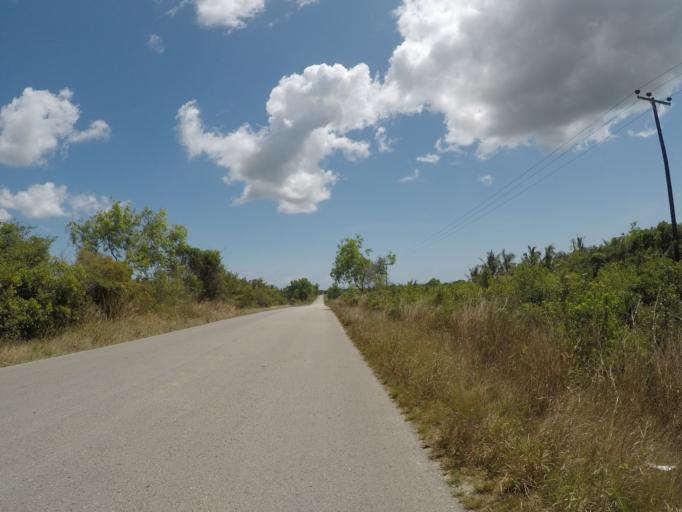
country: TZ
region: Zanzibar Central/South
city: Nganane
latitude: -6.2749
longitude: 39.4884
